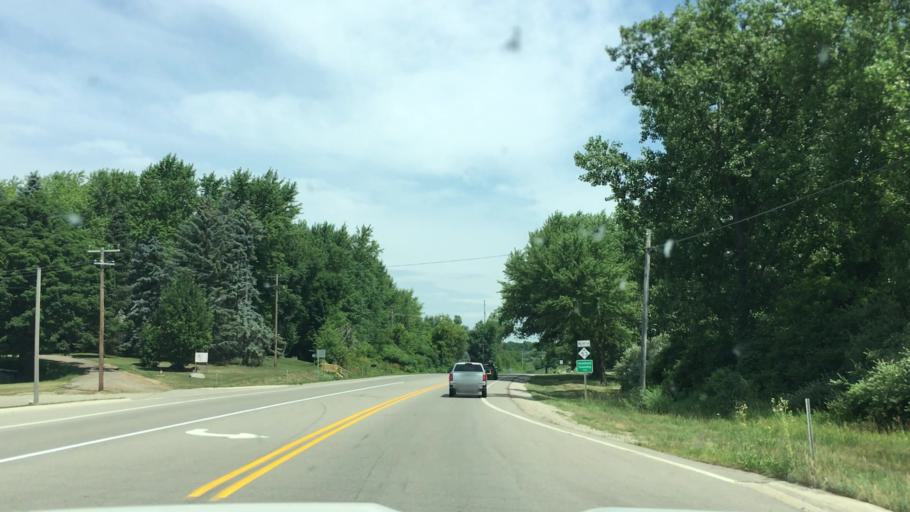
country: US
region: Michigan
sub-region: Lapeer County
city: Imlay City
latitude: 43.0657
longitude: -83.0744
